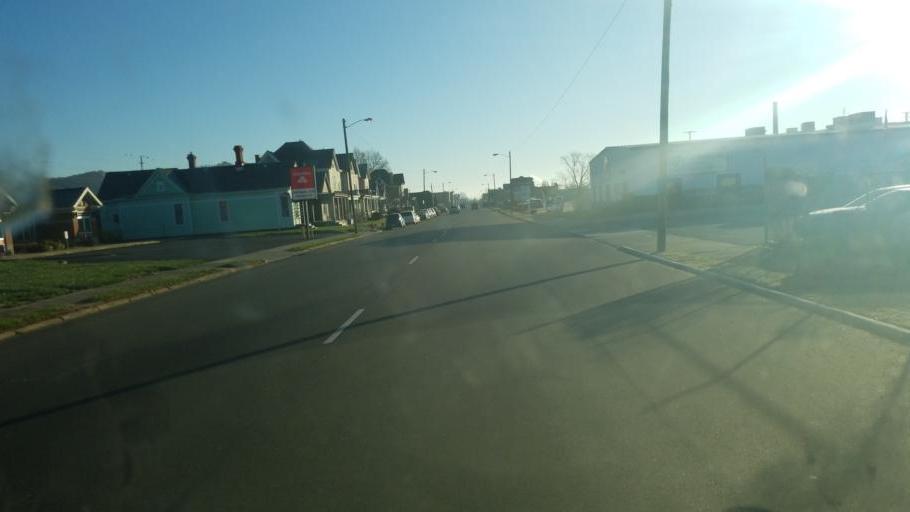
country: US
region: Ohio
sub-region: Scioto County
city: Portsmouth
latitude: 38.7389
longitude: -82.9826
